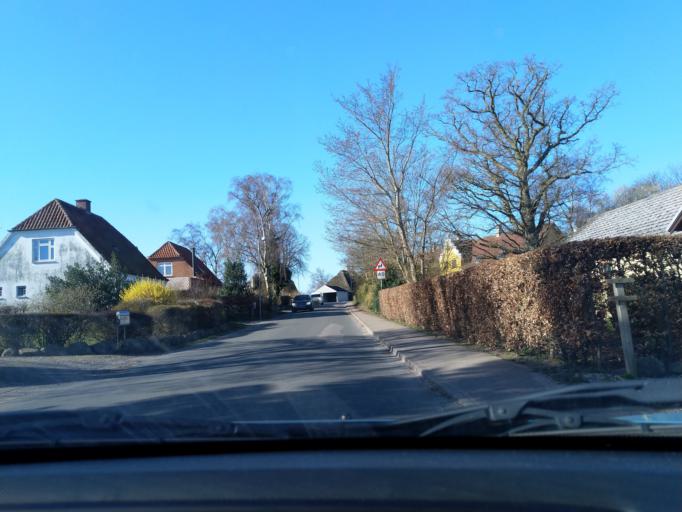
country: DK
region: Zealand
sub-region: Kalundborg Kommune
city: Kalundborg
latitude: 55.7331
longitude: 10.9624
